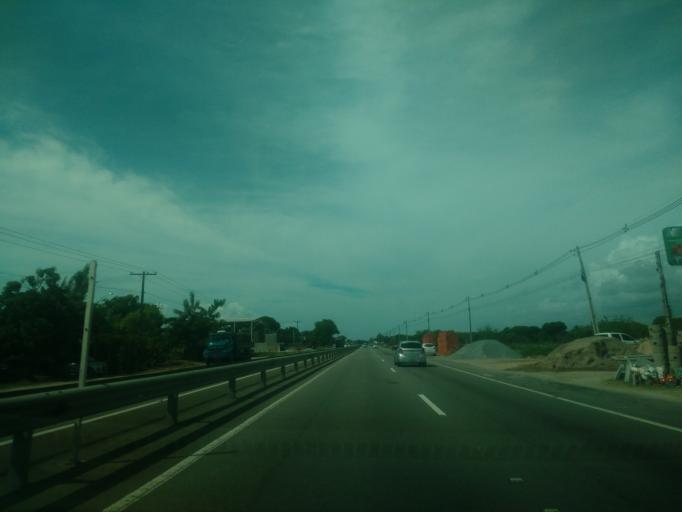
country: BR
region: Alagoas
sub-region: Marechal Deodoro
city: Marechal Deodoro
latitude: -9.7499
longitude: -35.8397
